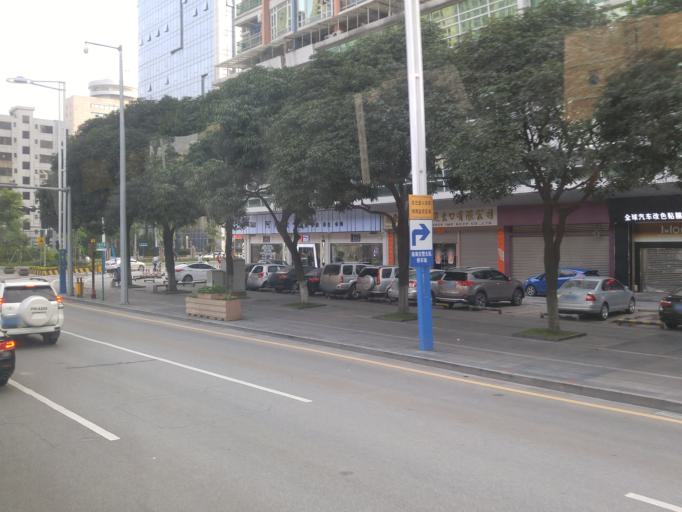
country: CN
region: Guangdong
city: Foshan
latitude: 23.0615
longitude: 113.1401
